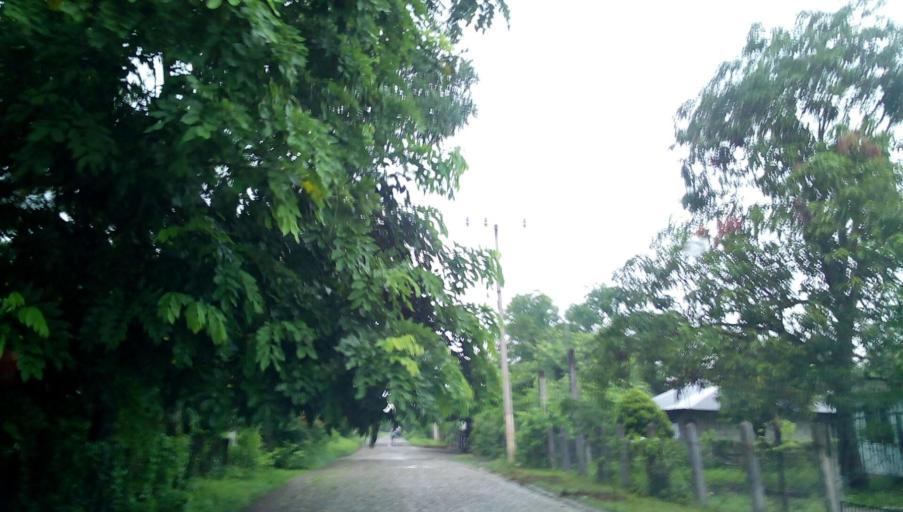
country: MX
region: Veracruz
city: Tempoal de Sanchez
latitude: 21.4186
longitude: -98.4250
